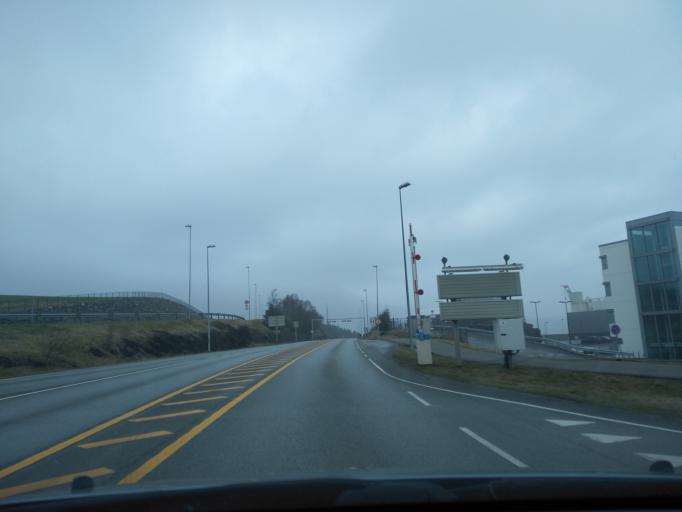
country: NO
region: Rogaland
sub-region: Randaberg
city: Randaberg
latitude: 59.0124
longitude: 5.6354
